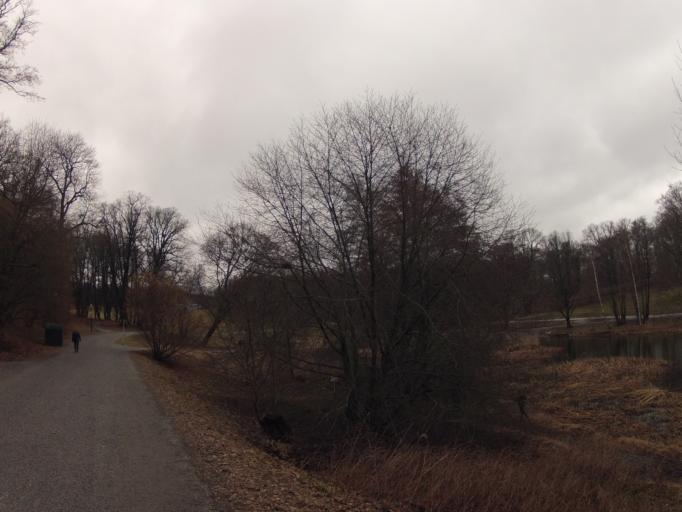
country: SE
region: Stockholm
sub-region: Norrtalje Kommun
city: Bergshamra
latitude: 59.3618
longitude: 18.0371
